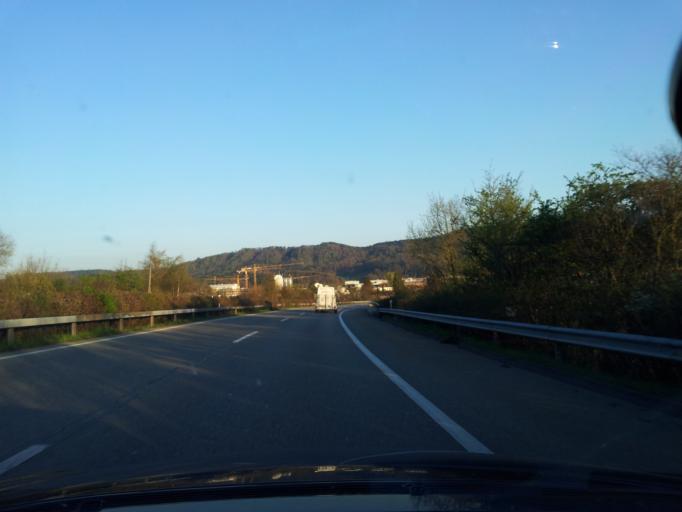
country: CH
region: Bern
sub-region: Bern-Mittelland District
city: Urtenen
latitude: 47.0239
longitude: 7.4854
